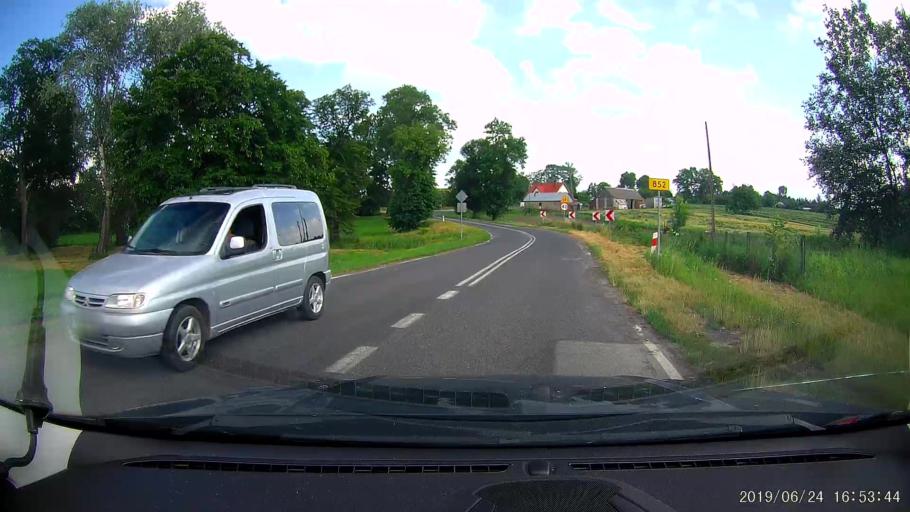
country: PL
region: Lublin Voivodeship
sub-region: Powiat tomaszowski
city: Telatyn
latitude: 50.5348
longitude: 23.8061
